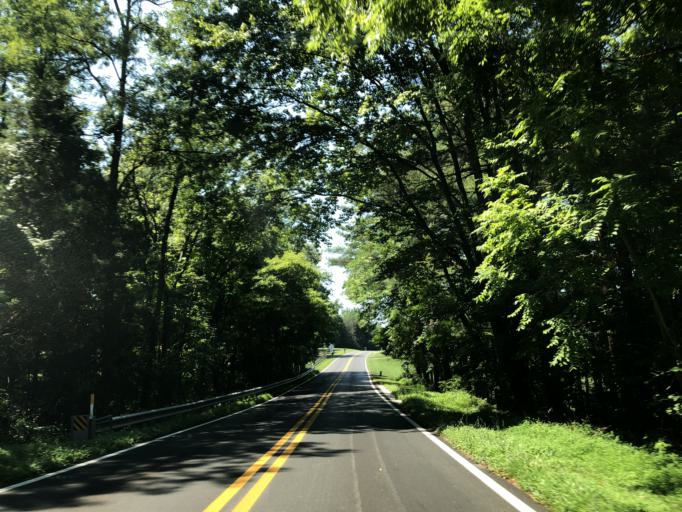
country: US
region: Maryland
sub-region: Carroll County
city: Eldersburg
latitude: 39.4401
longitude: -76.9558
